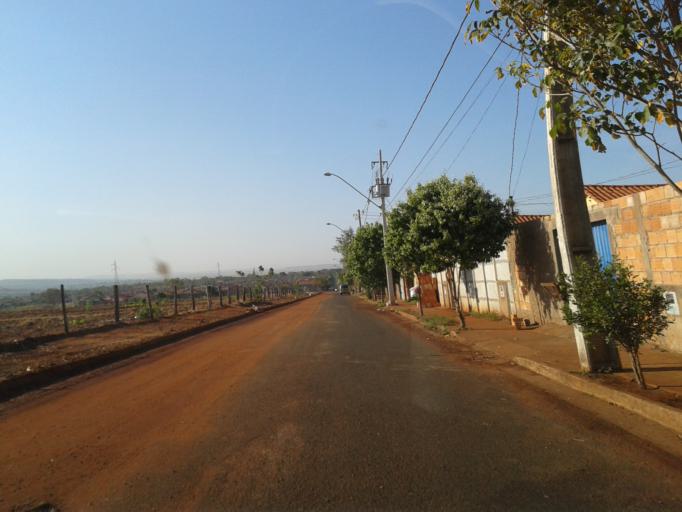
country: BR
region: Minas Gerais
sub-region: Ituiutaba
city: Ituiutaba
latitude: -18.9809
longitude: -49.4307
